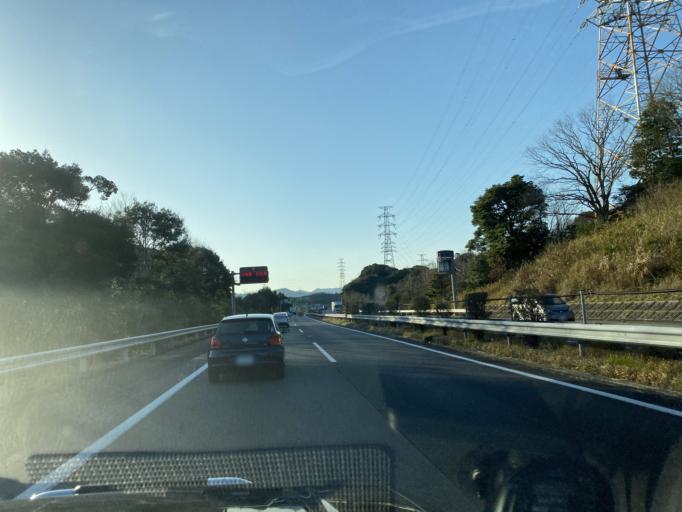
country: JP
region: Mie
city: Kameyama
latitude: 34.8360
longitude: 136.4247
